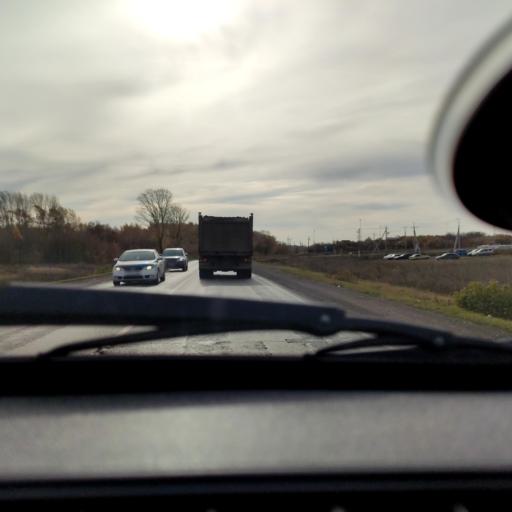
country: RU
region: Bashkortostan
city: Avdon
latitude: 54.7233
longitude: 55.8075
